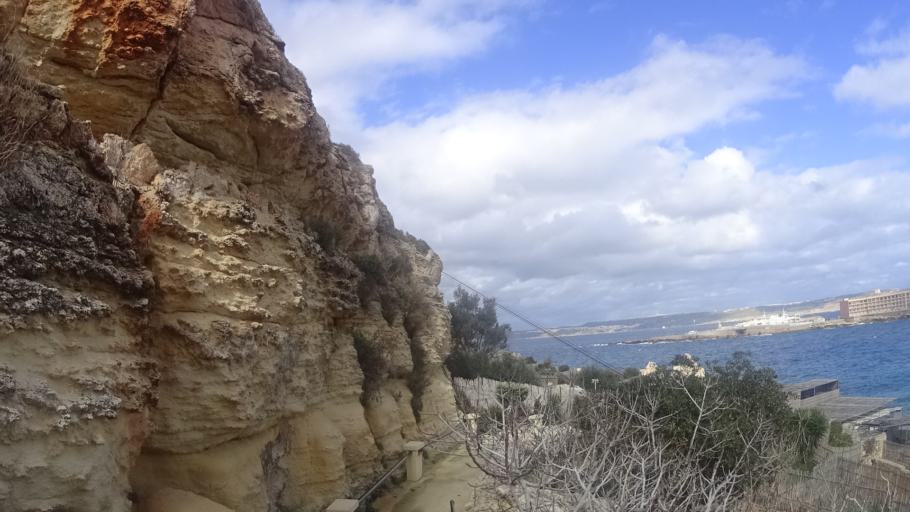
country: MT
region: Il-Mellieha
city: Mellieha
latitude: 35.9813
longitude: 14.3320
